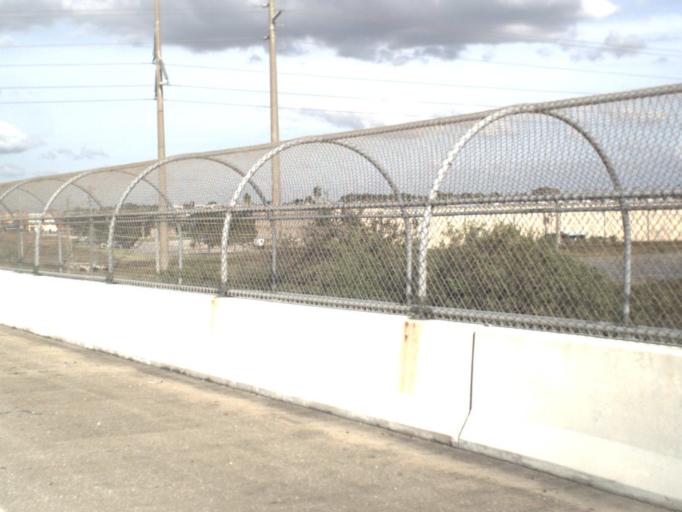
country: US
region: Florida
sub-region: Orange County
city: Oak Ridge
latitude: 28.4562
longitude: -81.4265
